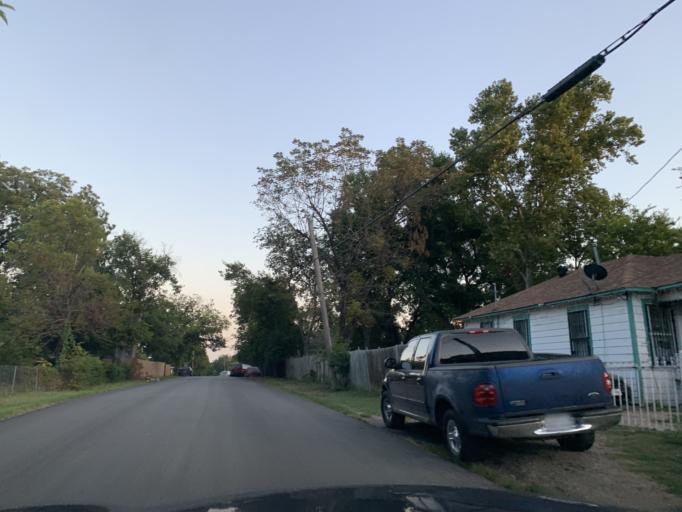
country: US
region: Texas
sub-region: Dallas County
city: Dallas
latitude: 32.7038
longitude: -96.8037
